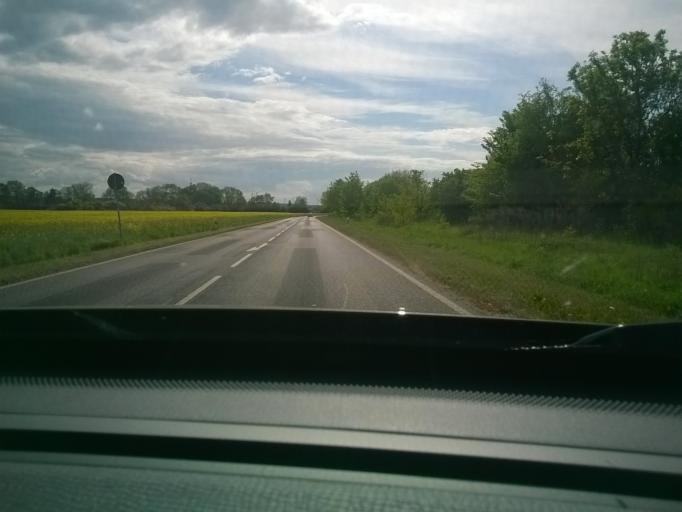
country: DE
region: Brandenburg
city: Wittstock
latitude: 53.1612
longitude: 12.5012
